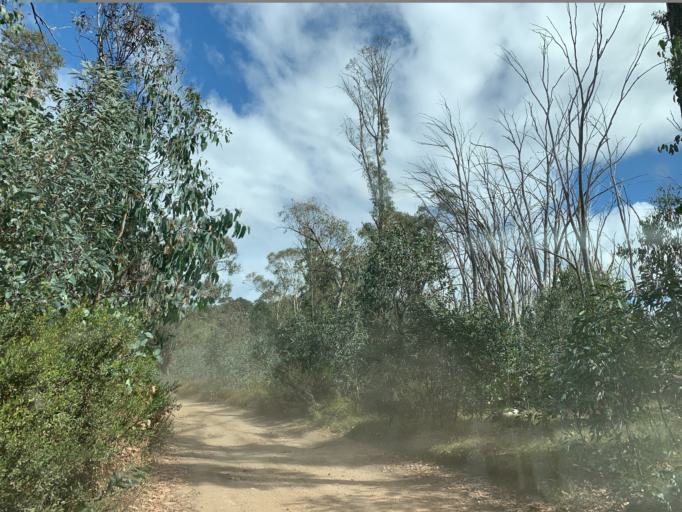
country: AU
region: Victoria
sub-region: Mansfield
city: Mansfield
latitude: -37.1016
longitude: 146.5434
